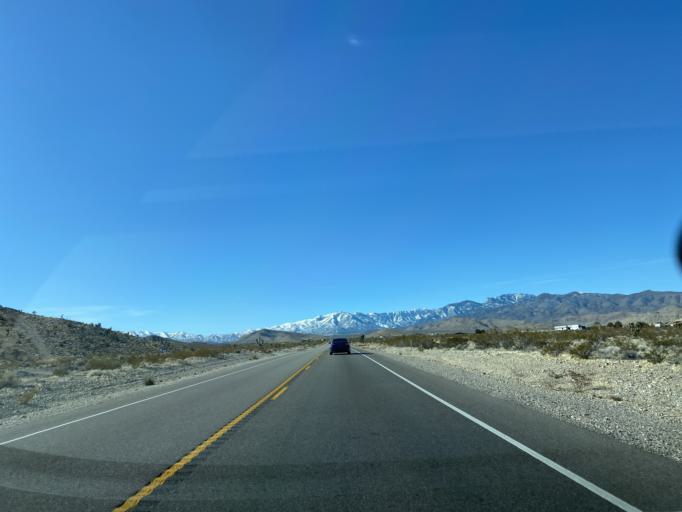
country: US
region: Nevada
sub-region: Clark County
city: Summerlin South
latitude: 36.3092
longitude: -115.3941
